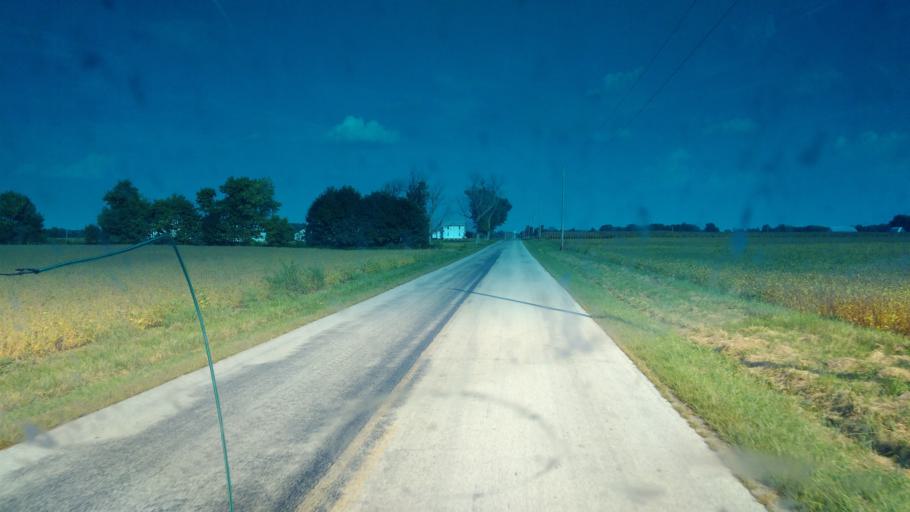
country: US
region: Ohio
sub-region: Wyandot County
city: Carey
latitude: 40.9051
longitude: -83.4069
